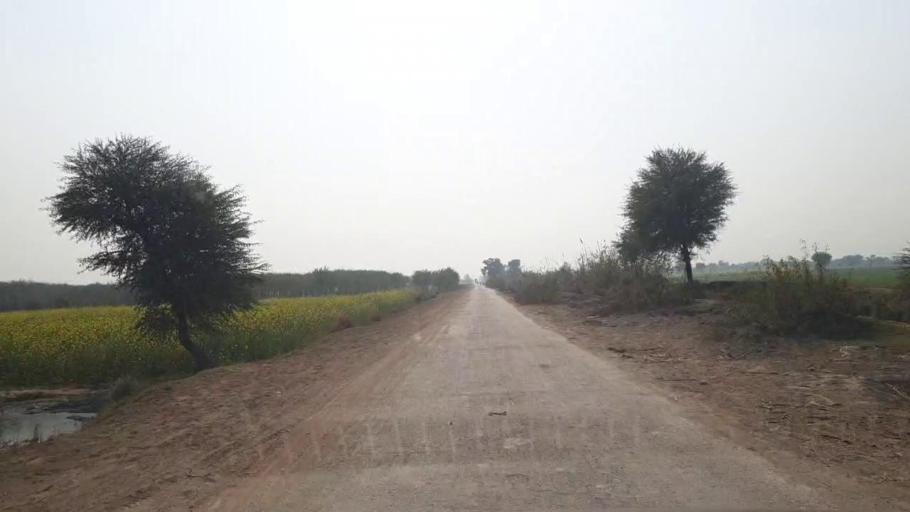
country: PK
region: Sindh
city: Hala
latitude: 25.9171
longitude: 68.4458
